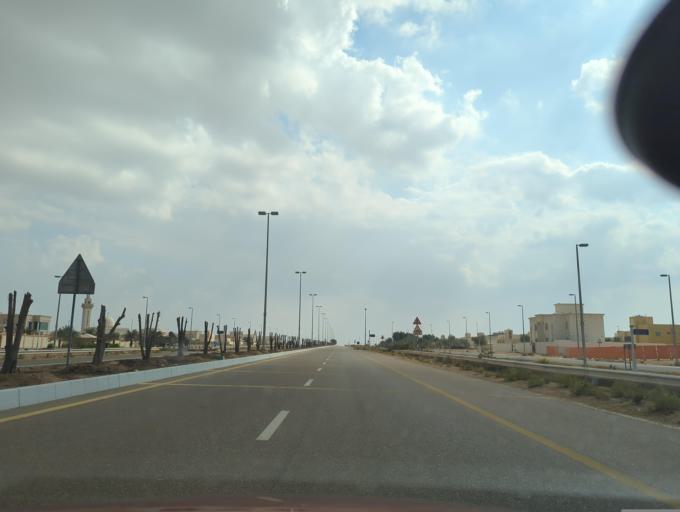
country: AE
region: Abu Dhabi
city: Abu Dhabi
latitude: 24.3725
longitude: 54.7161
